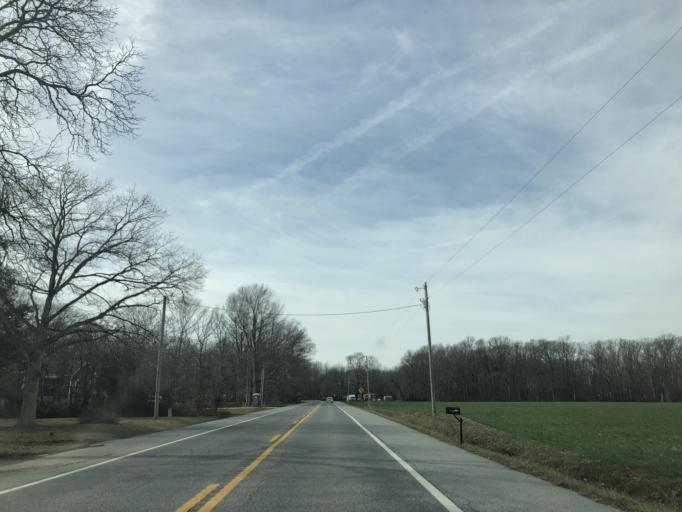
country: US
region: Delaware
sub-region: Kent County
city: Smyrna
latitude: 39.2808
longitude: -75.5542
